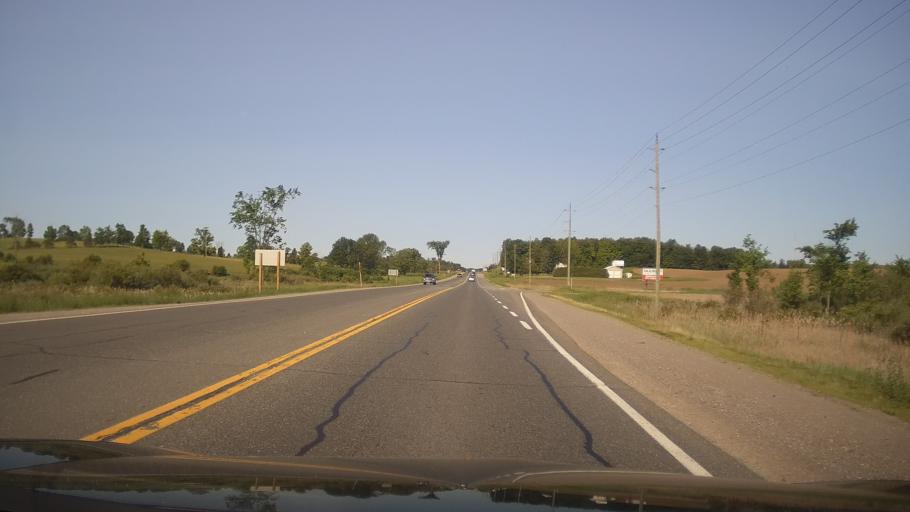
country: CA
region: Ontario
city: Peterborough
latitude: 44.3220
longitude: -78.1646
